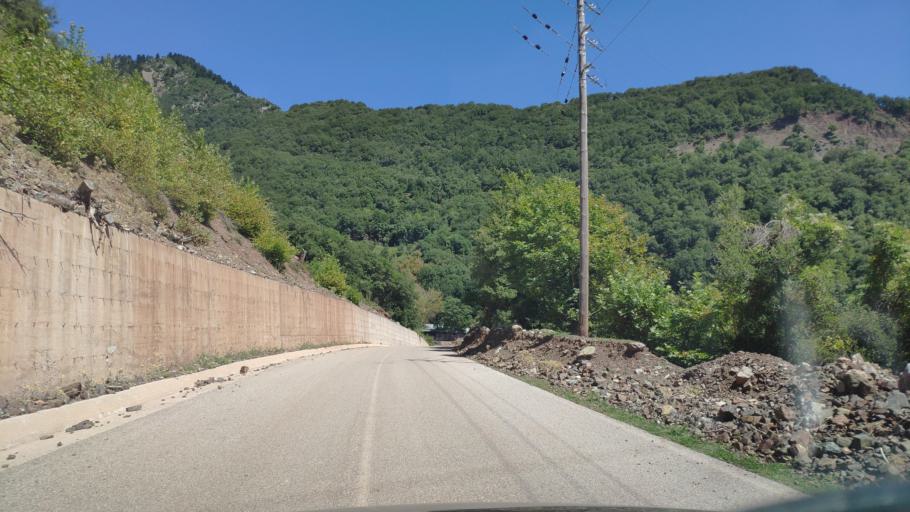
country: GR
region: Central Greece
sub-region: Nomos Evrytanias
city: Kerasochori
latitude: 39.0885
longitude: 21.5968
